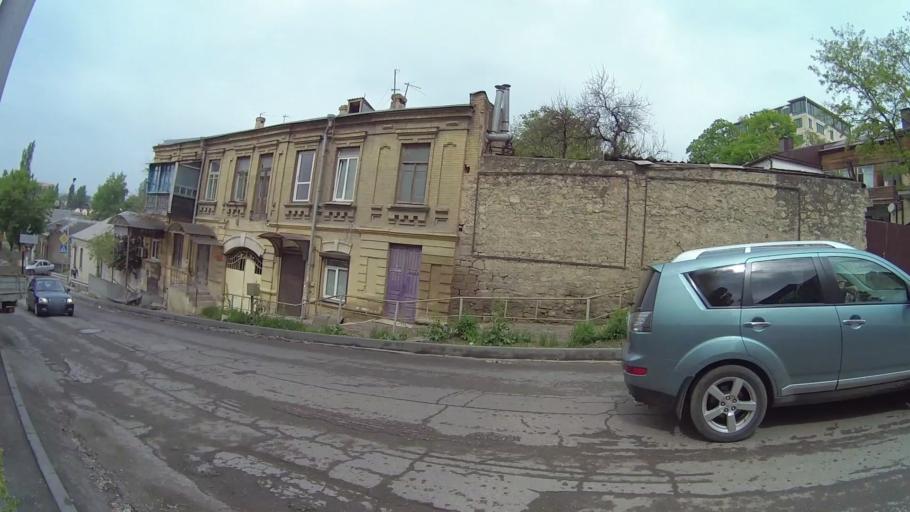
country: RU
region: Stavropol'skiy
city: Goryachevodskiy
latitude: 44.0345
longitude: 43.0753
